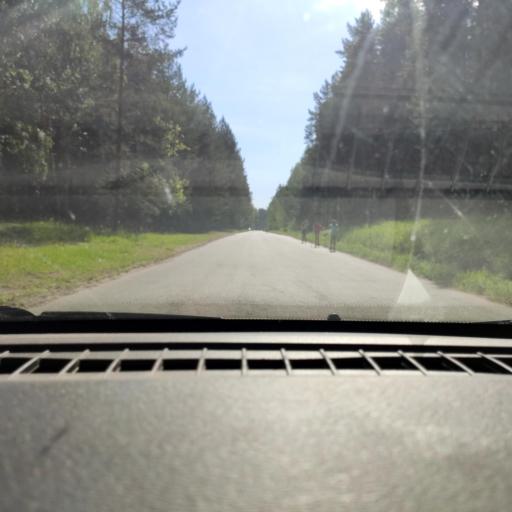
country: RU
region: Perm
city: Overyata
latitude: 57.9990
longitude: 55.8715
